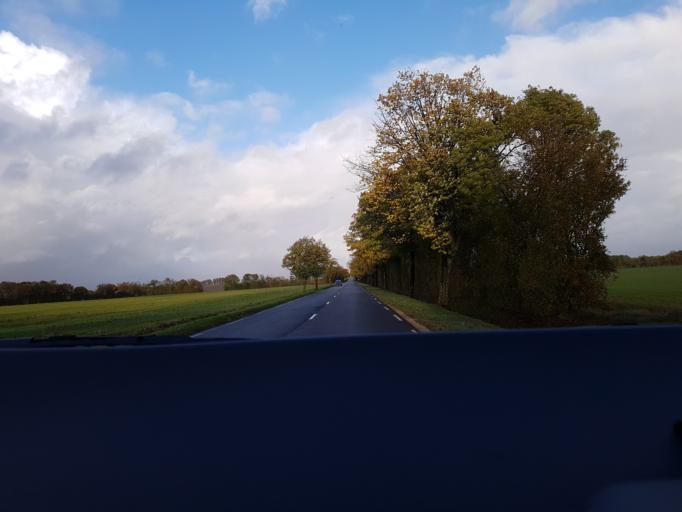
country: FR
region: Poitou-Charentes
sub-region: Departement des Deux-Sevres
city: Brioux-sur-Boutonne
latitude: 46.1101
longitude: -0.2553
